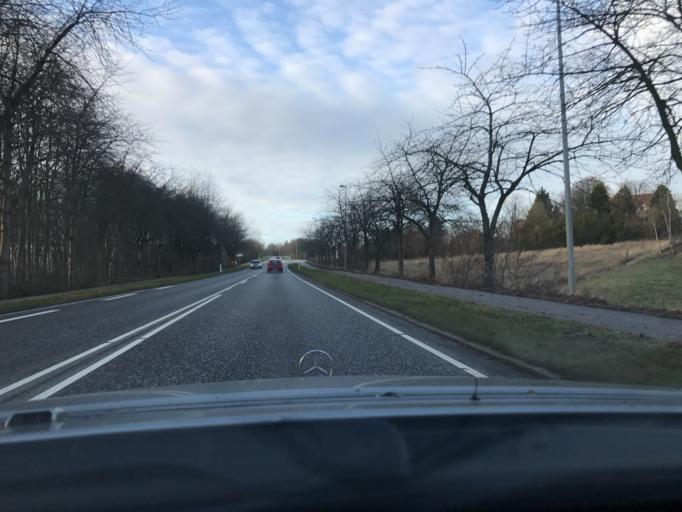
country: DK
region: South Denmark
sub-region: Sonderborg Kommune
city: Nordborg
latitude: 55.0370
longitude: 9.8096
